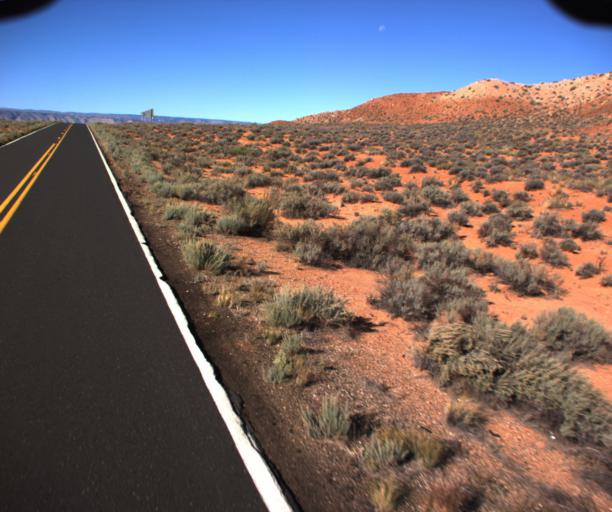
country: US
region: Arizona
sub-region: Coconino County
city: LeChee
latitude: 36.6860
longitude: -111.8348
